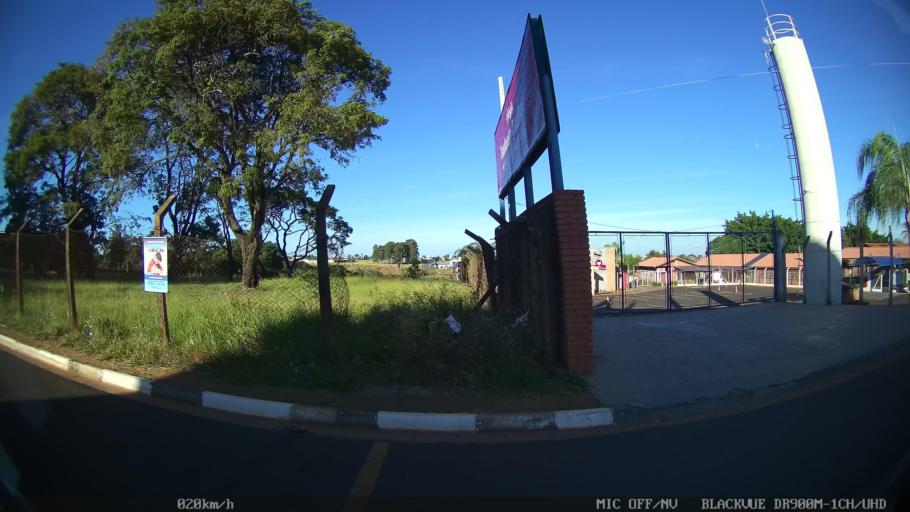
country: BR
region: Sao Paulo
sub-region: Franca
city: Franca
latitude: -20.5641
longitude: -47.4061
